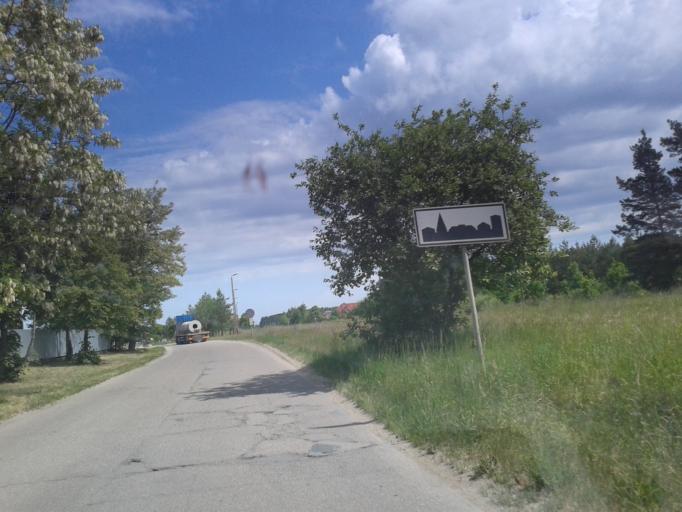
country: PL
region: Pomeranian Voivodeship
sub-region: Powiat koscierski
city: Karsin
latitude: 53.8941
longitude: 17.9250
